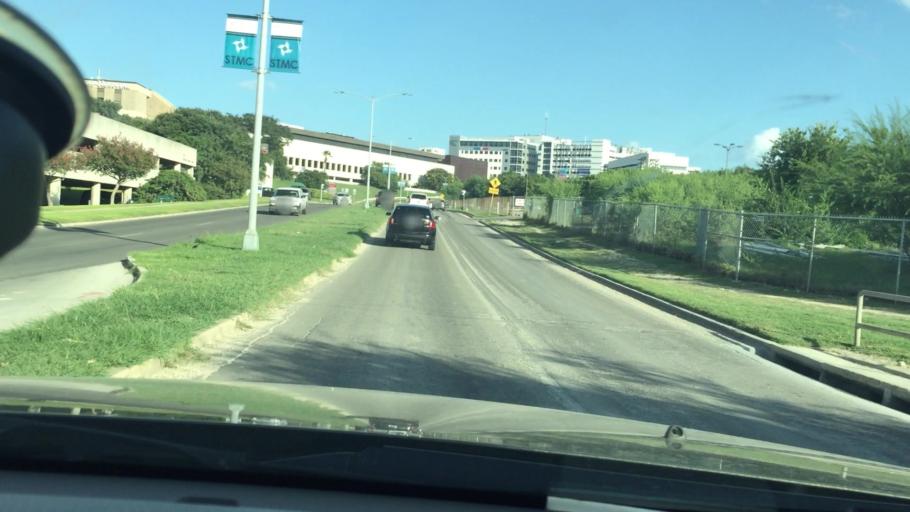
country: US
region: Texas
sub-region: Bexar County
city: Balcones Heights
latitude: 29.5125
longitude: -98.5770
